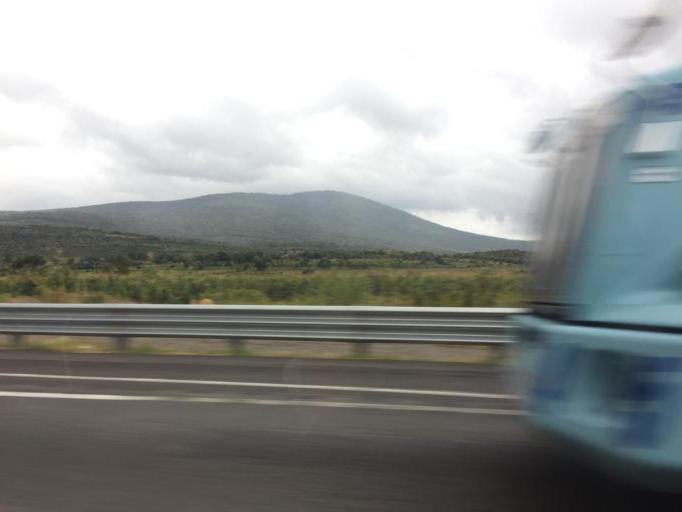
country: MX
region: Jalisco
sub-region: Zapotlanejo
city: La Mezquitera
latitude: 20.5482
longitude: -103.0353
